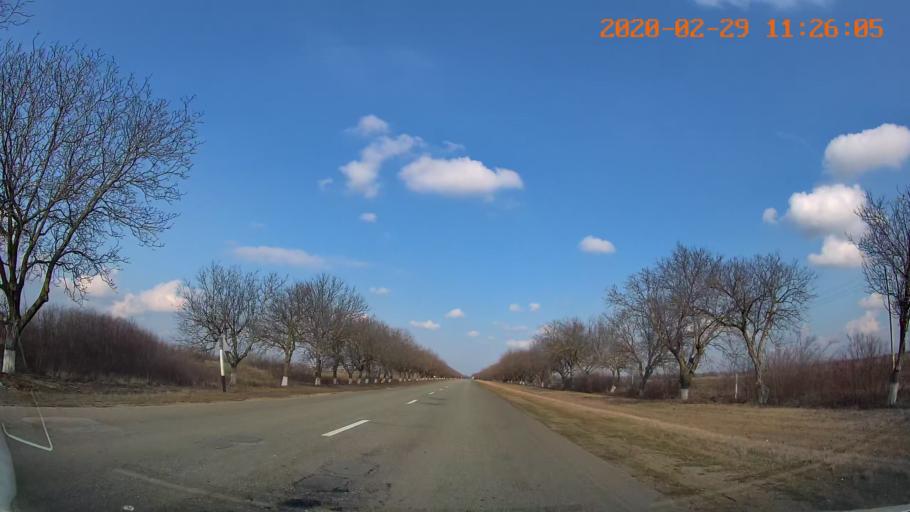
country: MD
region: Telenesti
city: Cocieri
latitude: 47.4480
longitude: 29.1476
